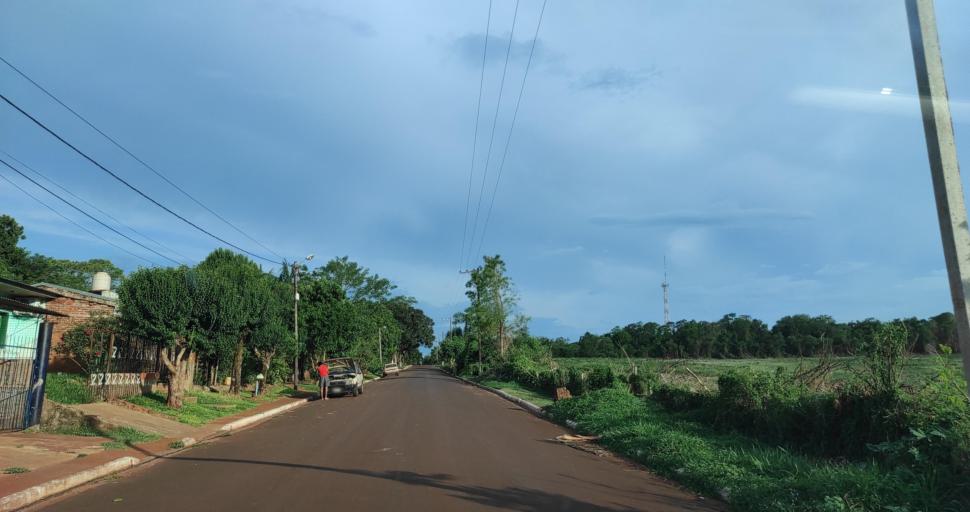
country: AR
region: Misiones
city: Santo Pipo
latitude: -27.1403
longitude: -55.4141
